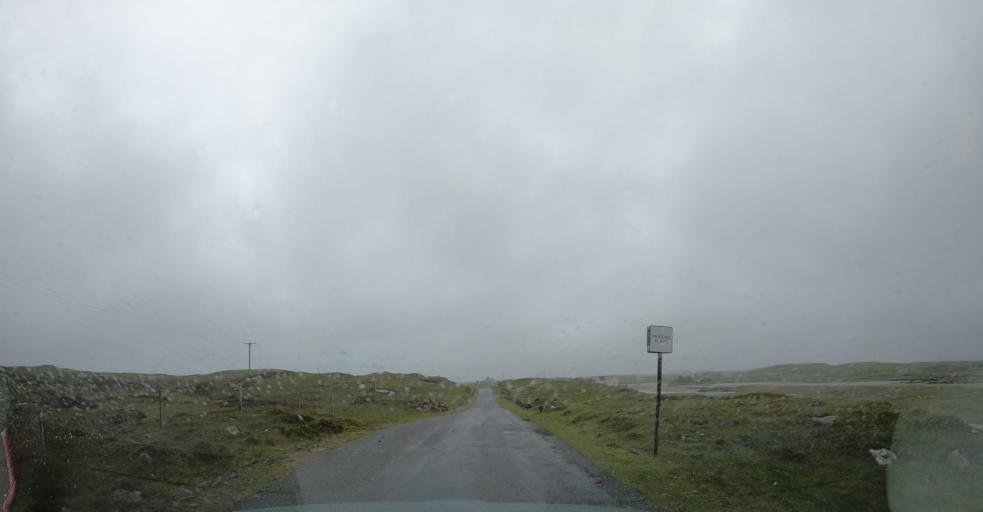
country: GB
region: Scotland
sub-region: Eilean Siar
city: Benbecula
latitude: 57.4978
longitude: -7.2419
